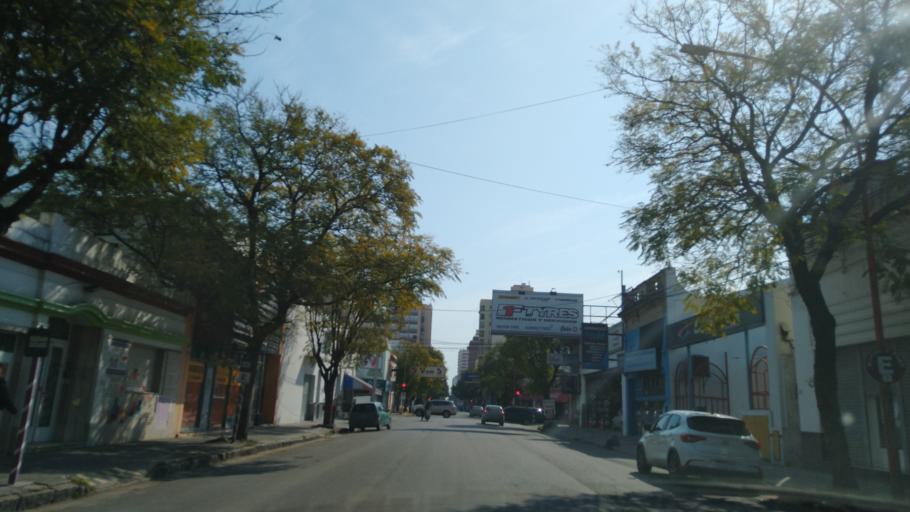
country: AR
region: Buenos Aires
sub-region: Partido de Bahia Blanca
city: Bahia Blanca
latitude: -38.7254
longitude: -62.2610
